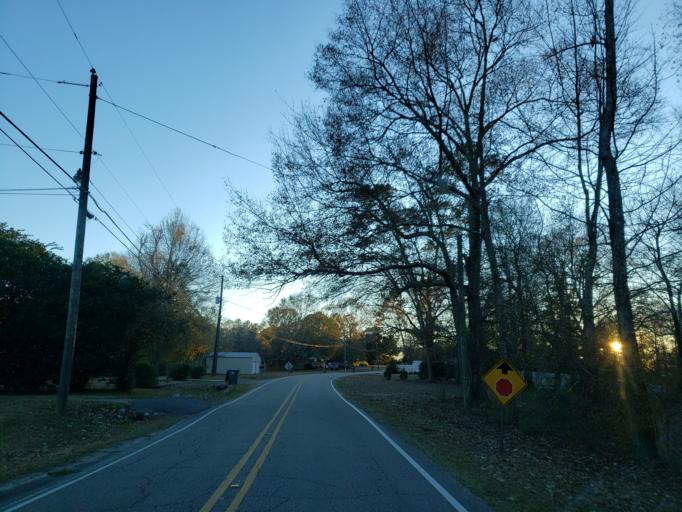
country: US
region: Mississippi
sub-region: Forrest County
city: Rawls Springs
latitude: 31.4256
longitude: -89.3354
